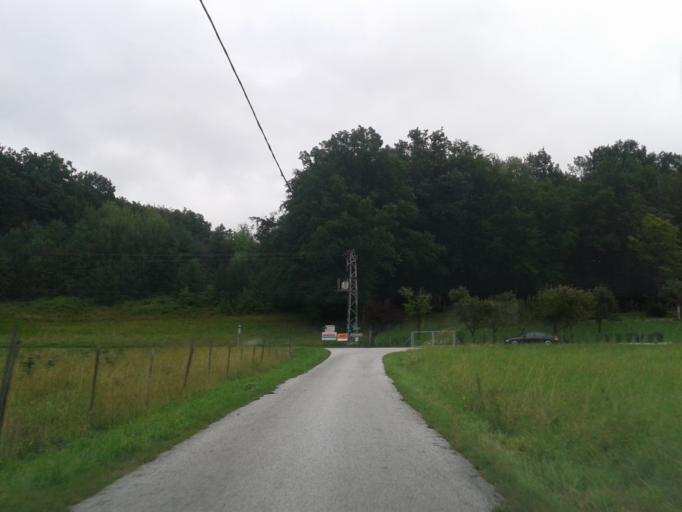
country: AT
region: Styria
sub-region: Politischer Bezirk Weiz
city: Sankt Ruprecht an der Raab
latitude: 47.1265
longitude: 15.6535
